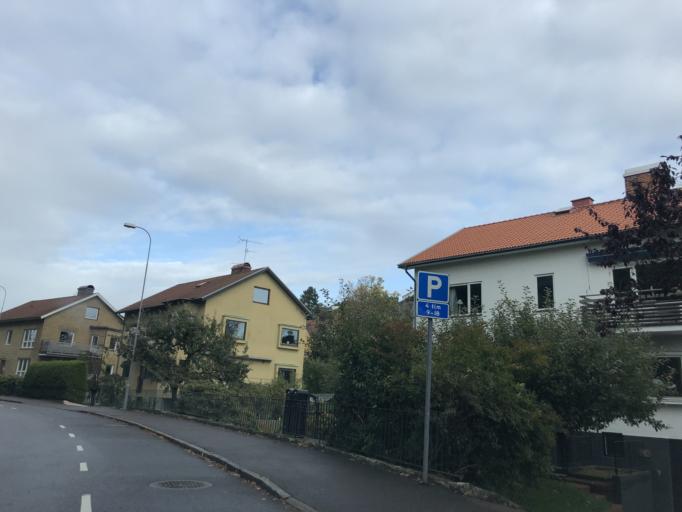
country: SE
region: Vaestra Goetaland
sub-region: Goteborg
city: Majorna
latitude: 57.6710
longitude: 11.8712
